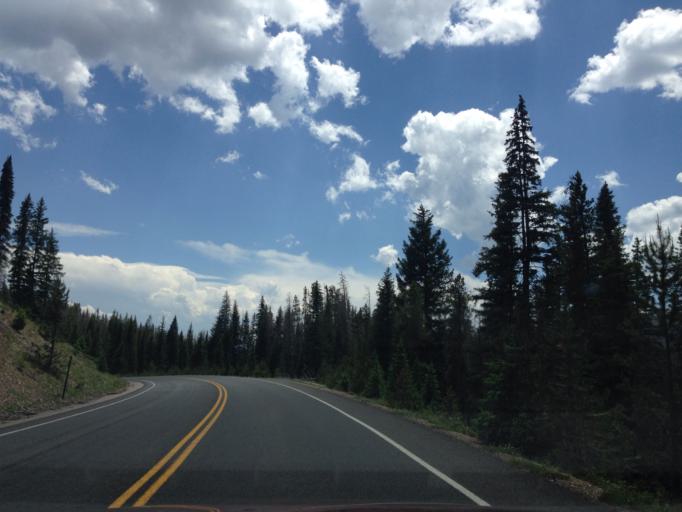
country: US
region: Colorado
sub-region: Grand County
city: Granby
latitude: 40.3442
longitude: -105.8580
